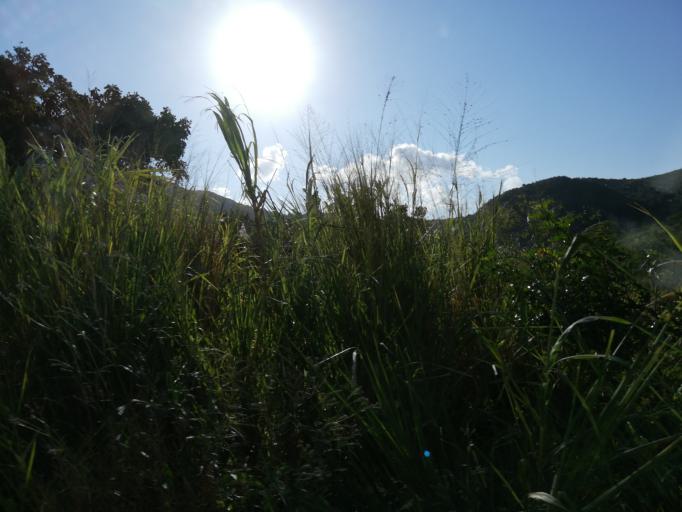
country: MU
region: Moka
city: Saint Pierre
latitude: -20.2094
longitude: 57.5259
